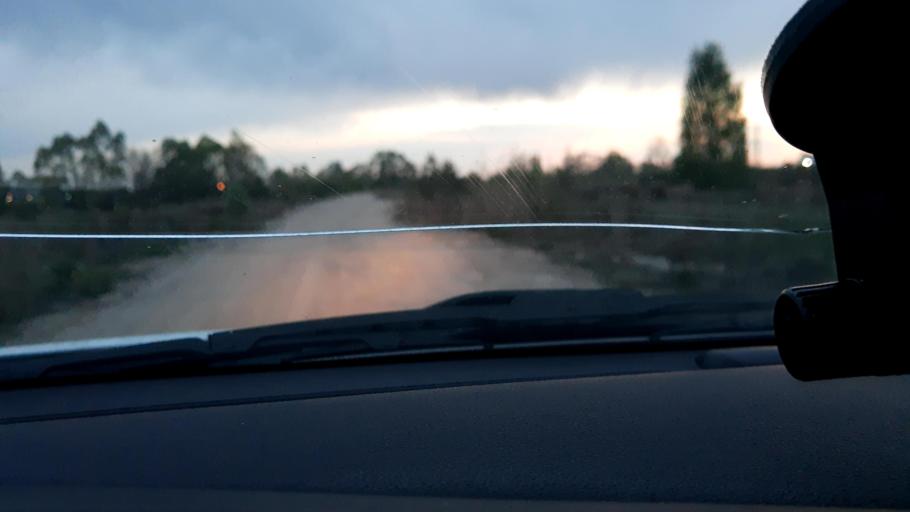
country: RU
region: Bashkortostan
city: Kabakovo
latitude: 54.6589
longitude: 56.0868
